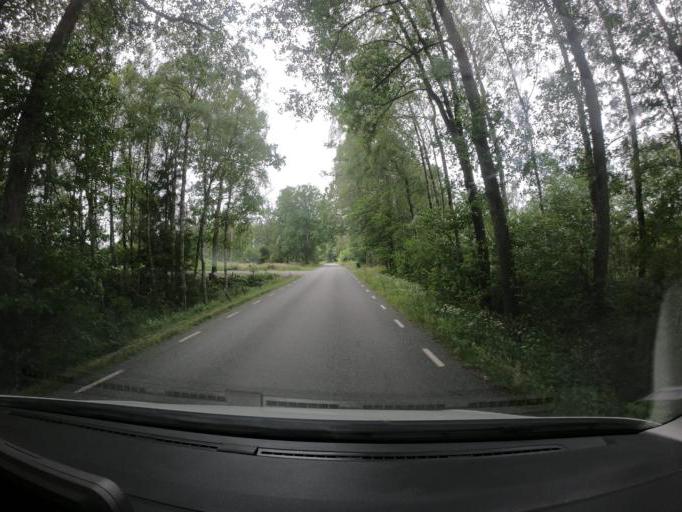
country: SE
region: Skane
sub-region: Hoors Kommun
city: Hoeoer
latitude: 56.0590
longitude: 13.5318
